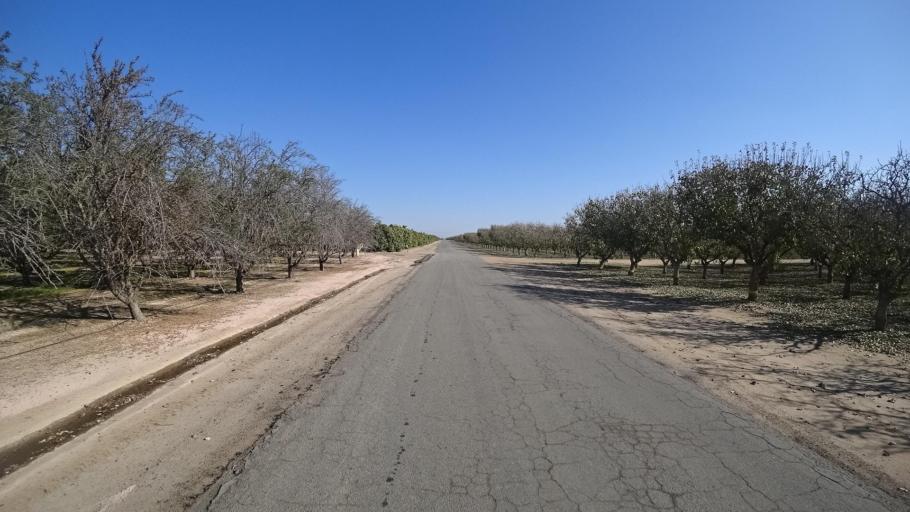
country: US
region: California
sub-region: Kern County
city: McFarland
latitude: 35.6456
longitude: -119.1782
